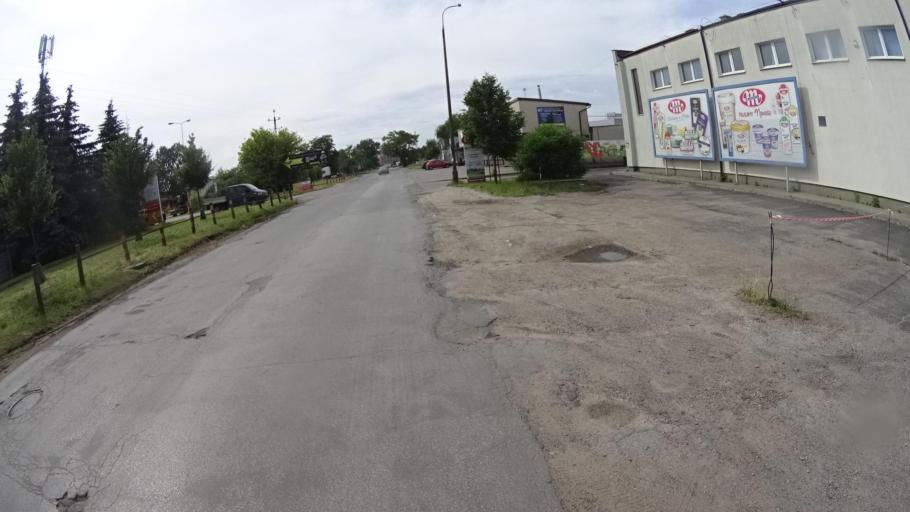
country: PL
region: Masovian Voivodeship
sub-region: Warszawa
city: Wlochy
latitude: 52.1904
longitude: 20.9382
